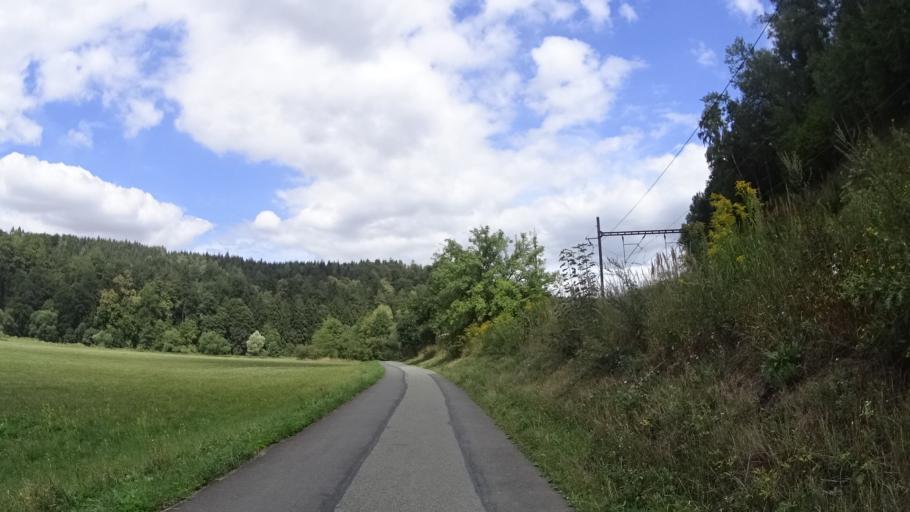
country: CZ
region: Pardubicky
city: Brandys nad Orlici
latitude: 49.9881
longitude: 16.3344
